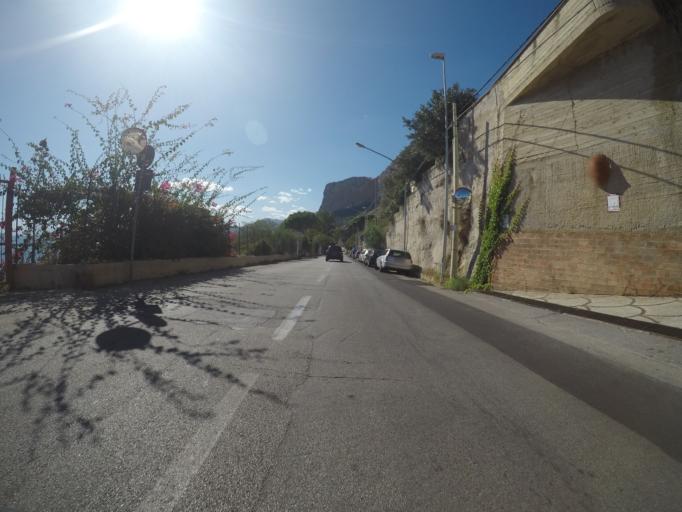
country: IT
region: Sicily
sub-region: Palermo
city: Palermo
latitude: 38.1737
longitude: 13.3661
